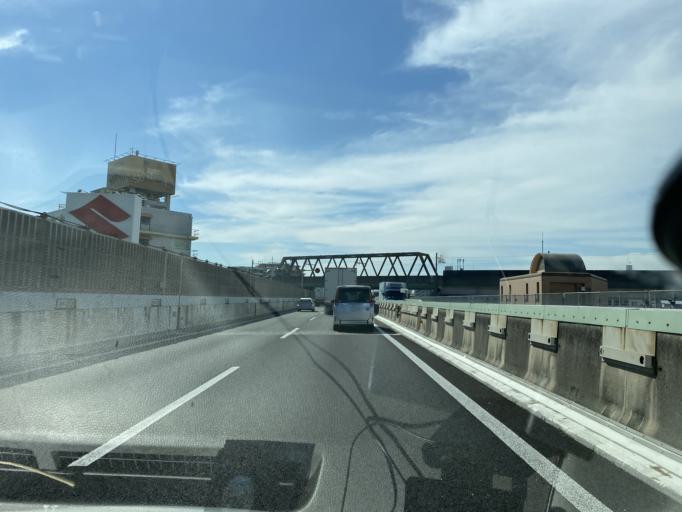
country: JP
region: Osaka
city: Ibaraki
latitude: 34.8067
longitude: 135.5619
